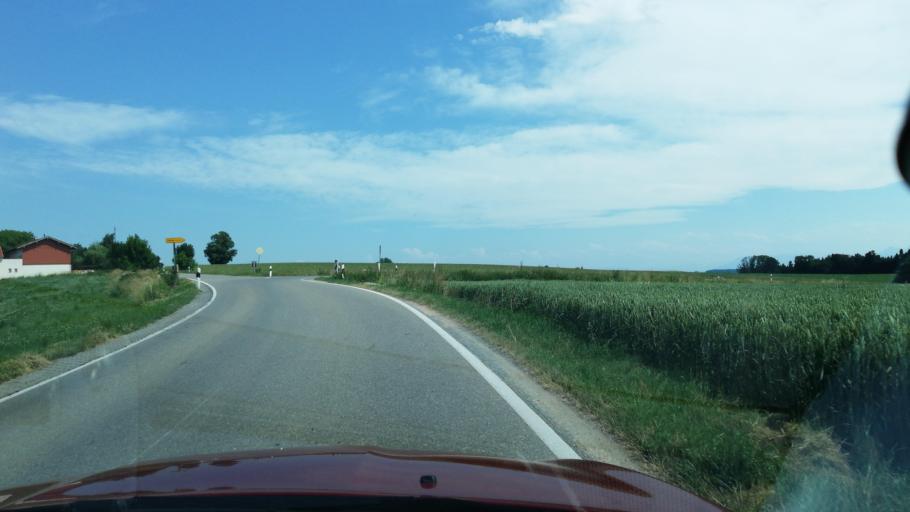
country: DE
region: Bavaria
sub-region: Upper Bavaria
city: Garching an der Alz
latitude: 48.1211
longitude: 12.5942
